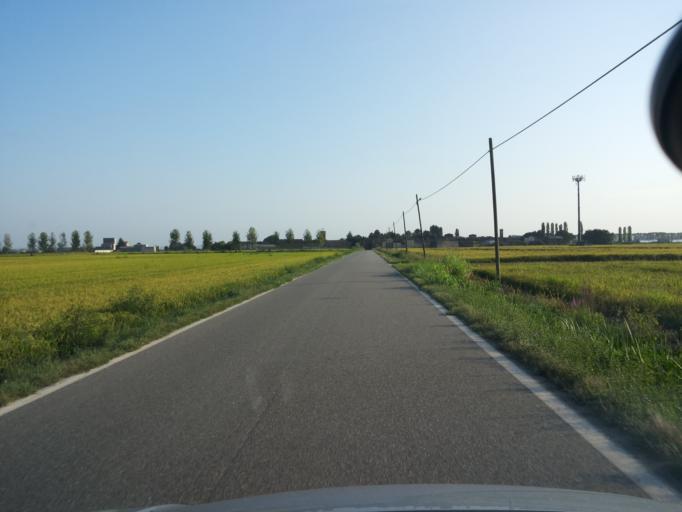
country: IT
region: Piedmont
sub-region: Provincia di Vercelli
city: Sali Vercellese
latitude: 45.3153
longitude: 8.3314
